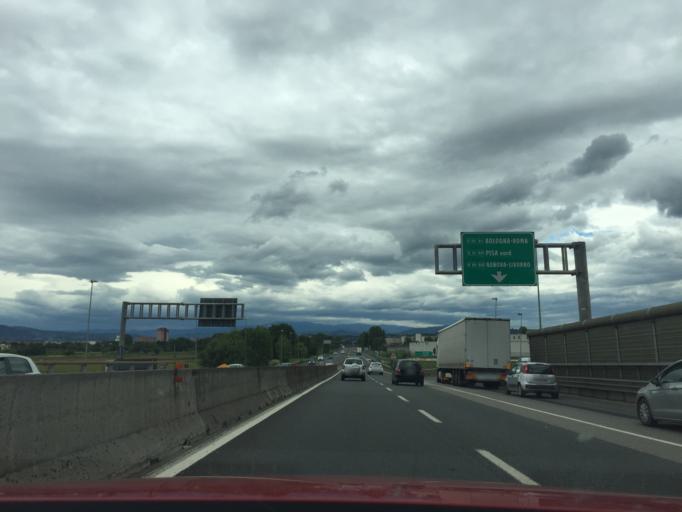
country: IT
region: Tuscany
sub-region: Province of Florence
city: Mantignano-Ugnano
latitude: 43.7724
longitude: 11.1651
